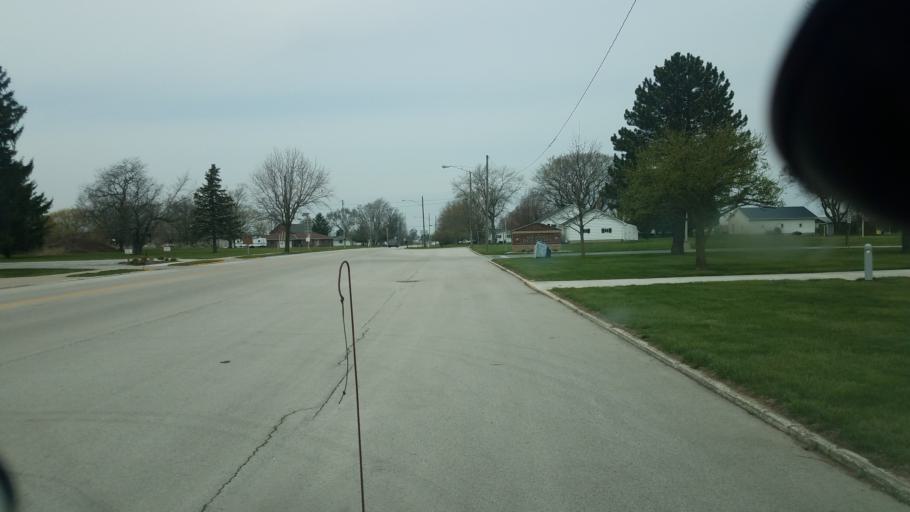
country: US
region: Ohio
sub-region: Wyandot County
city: Carey
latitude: 41.0544
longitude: -83.3207
